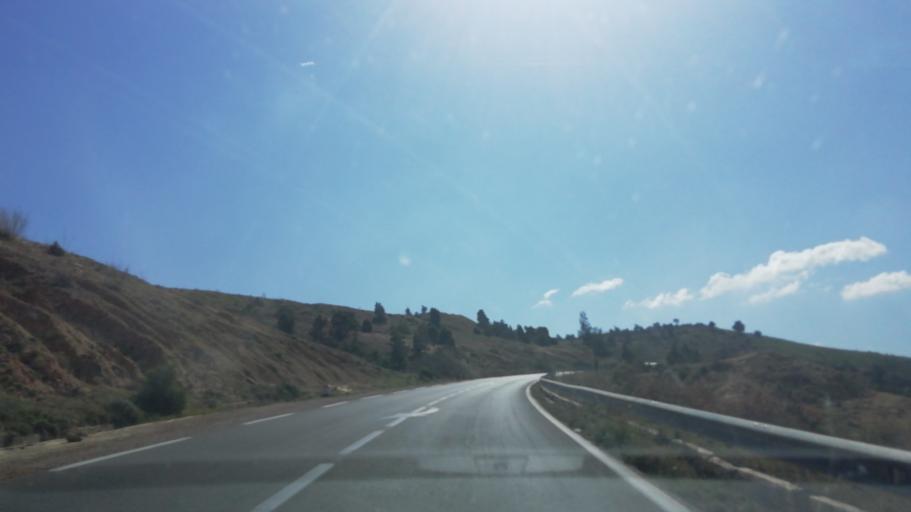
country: DZ
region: Mascara
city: Mascara
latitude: 35.4947
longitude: 0.1336
